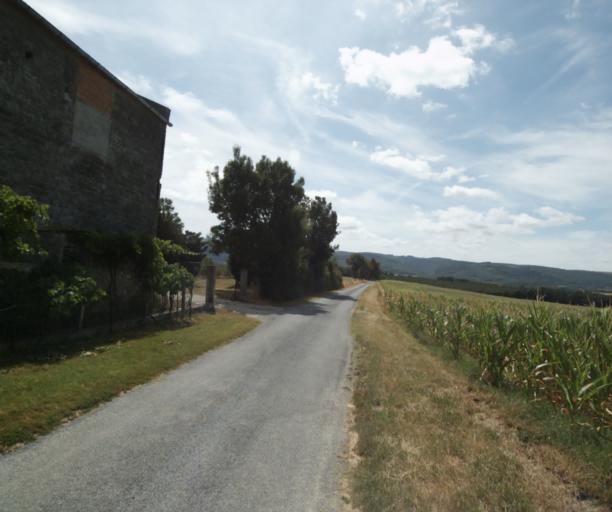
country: FR
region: Midi-Pyrenees
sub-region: Departement du Tarn
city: Dourgne
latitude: 43.4938
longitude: 2.0952
